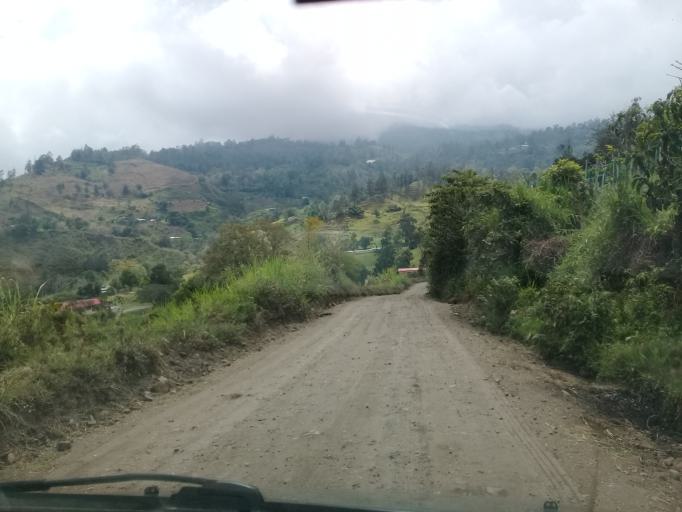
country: CO
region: Cundinamarca
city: Caqueza
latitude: 4.4116
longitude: -73.9835
